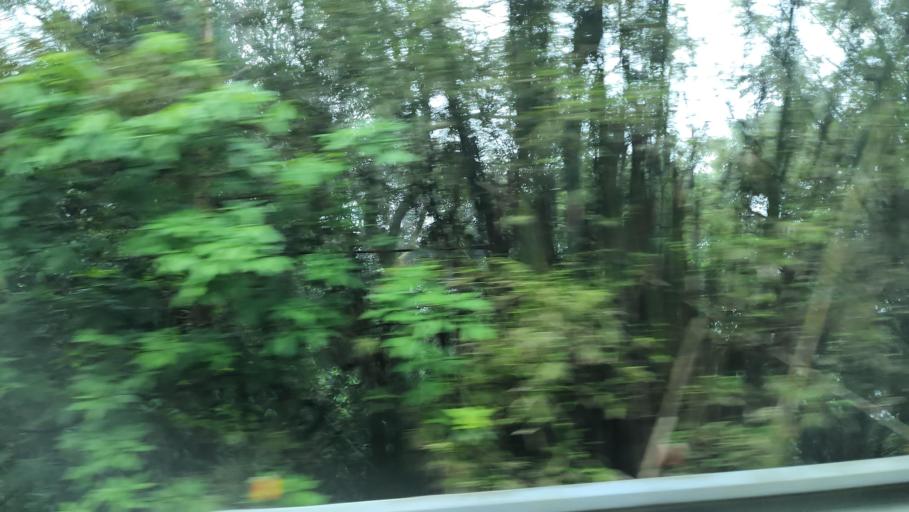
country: TW
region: Taipei
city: Taipei
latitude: 25.1423
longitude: 121.6024
